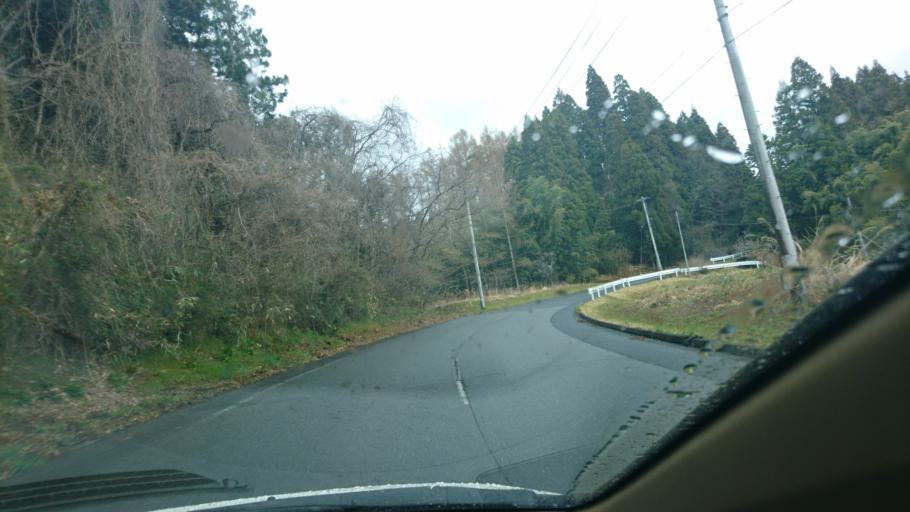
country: JP
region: Iwate
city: Ichinoseki
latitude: 38.9334
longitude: 141.3168
